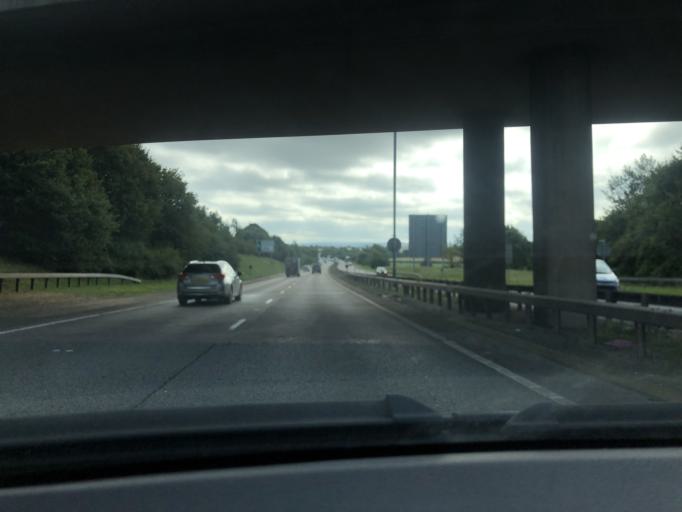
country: GB
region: England
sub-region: Devon
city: Topsham
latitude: 50.7306
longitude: -3.4448
